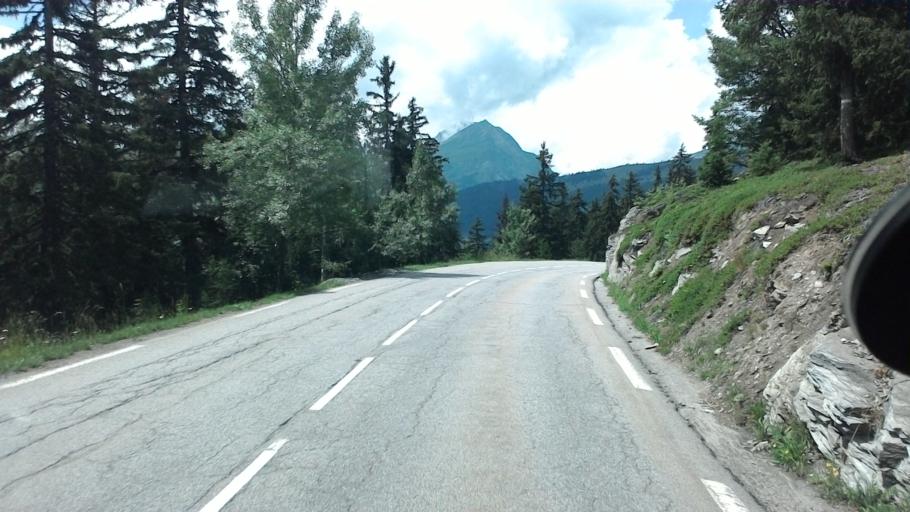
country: FR
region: Rhone-Alpes
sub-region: Departement de la Savoie
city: Seez
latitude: 45.6233
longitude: 6.8425
